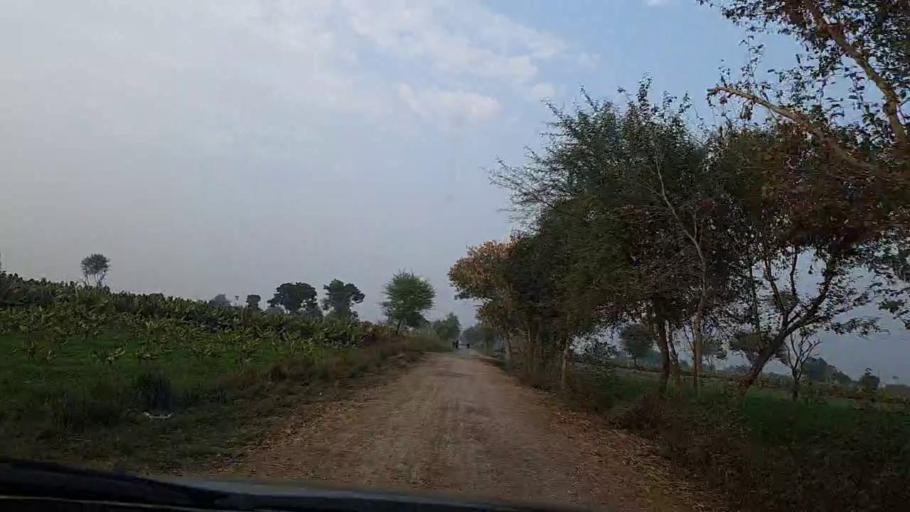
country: PK
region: Sindh
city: Nawabshah
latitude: 26.2874
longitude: 68.3212
